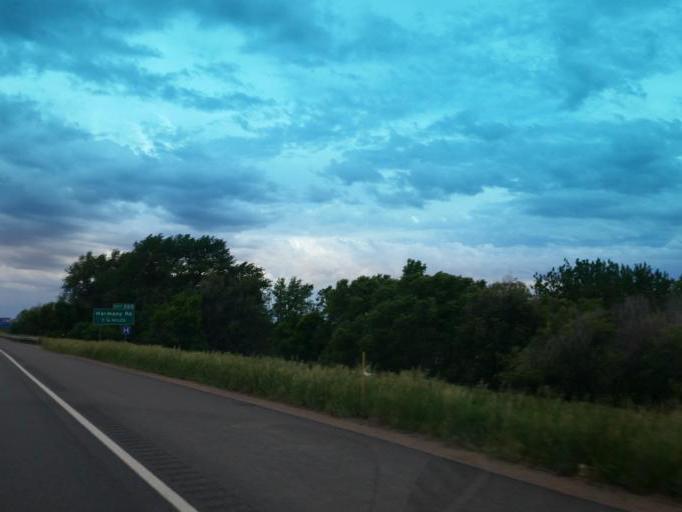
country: US
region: Colorado
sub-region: Larimer County
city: Fort Collins
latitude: 40.5448
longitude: -104.9975
